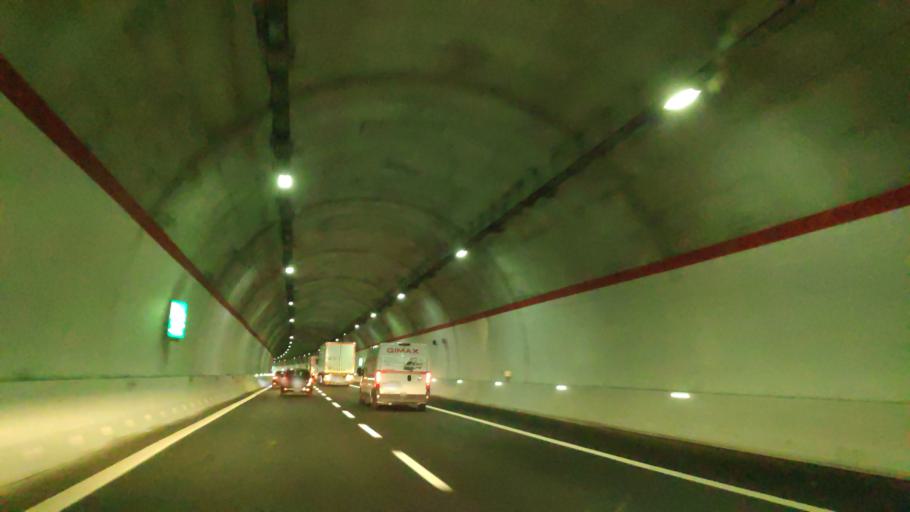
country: IT
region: Campania
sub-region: Provincia di Salerno
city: Casalbuono
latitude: 40.1882
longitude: 15.7075
